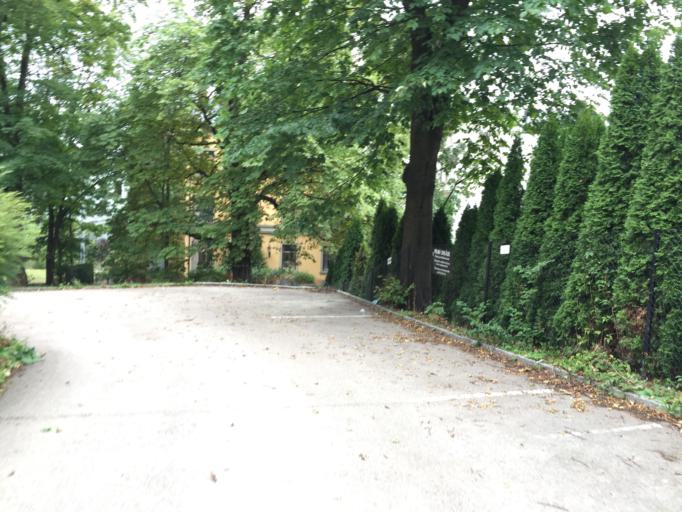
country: NO
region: Oslo
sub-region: Oslo
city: Oslo
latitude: 59.9122
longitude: 10.7175
